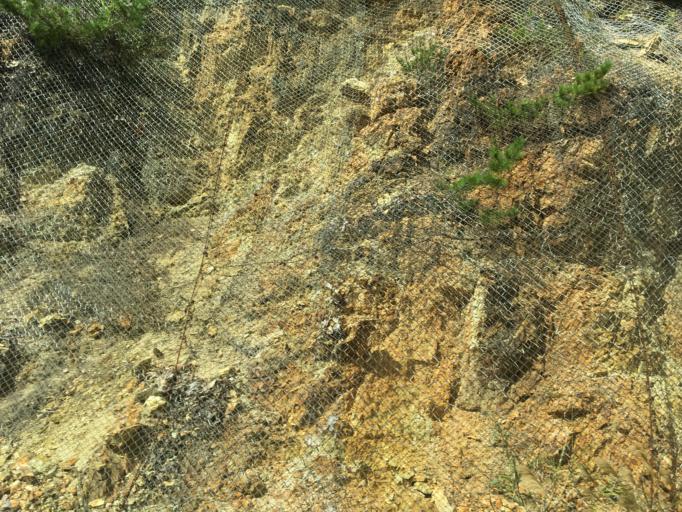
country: JP
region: Aomori
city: Shimokizukuri
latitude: 40.6634
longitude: 139.9377
